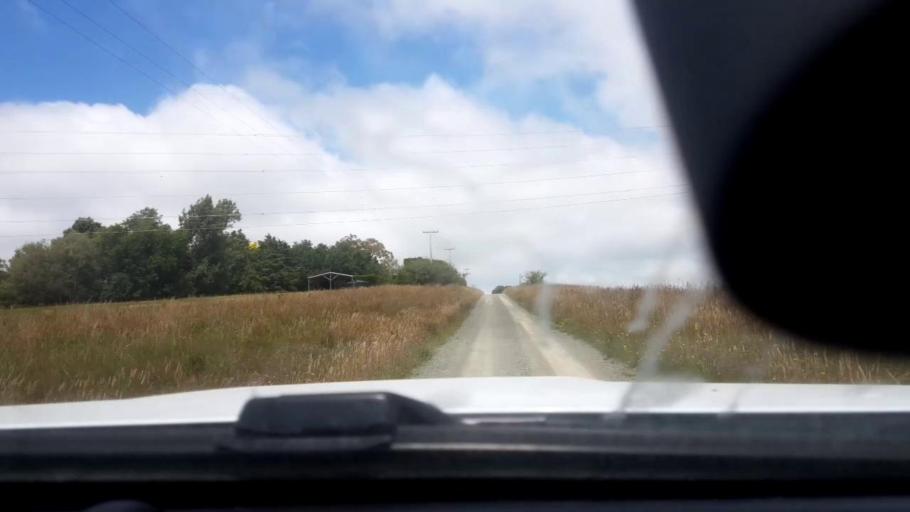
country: NZ
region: Canterbury
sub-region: Timaru District
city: Pleasant Point
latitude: -44.1541
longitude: 171.1499
